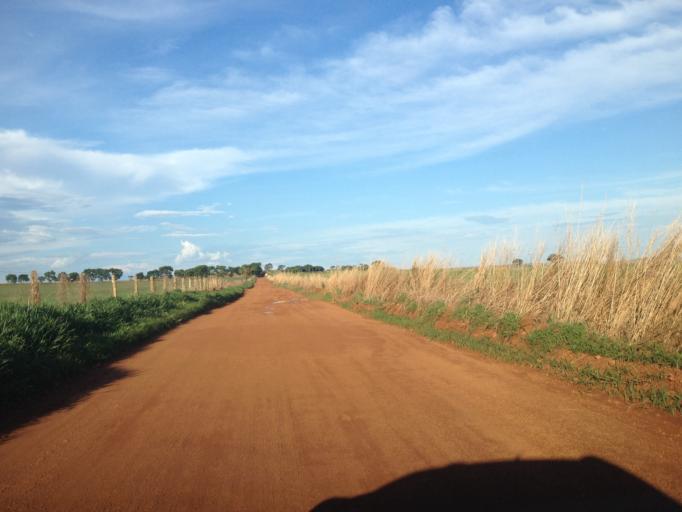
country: BR
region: Goias
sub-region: Abadiania
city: Abadiania
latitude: -15.9950
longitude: -48.5404
